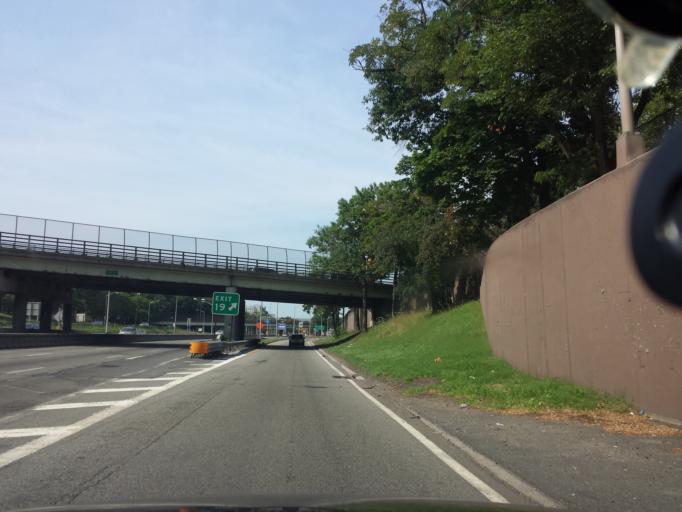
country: US
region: New York
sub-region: Kings County
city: Bensonhurst
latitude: 40.6248
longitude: -74.0194
